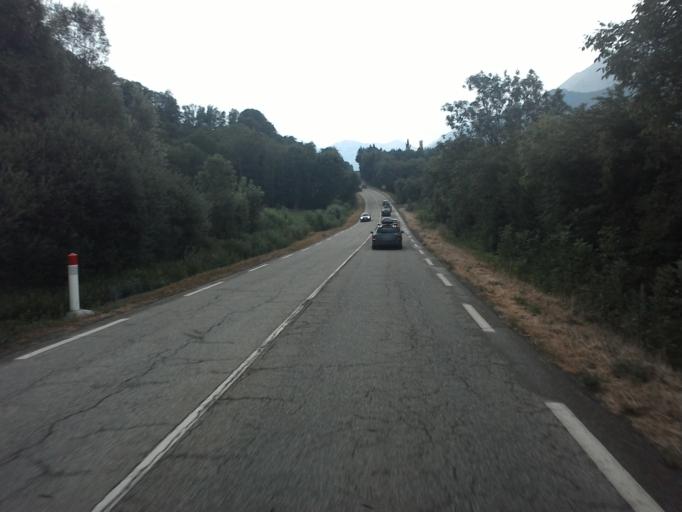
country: FR
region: Provence-Alpes-Cote d'Azur
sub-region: Departement des Hautes-Alpes
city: Saint-Bonnet-en-Champsaur
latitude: 44.7896
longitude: 5.9815
